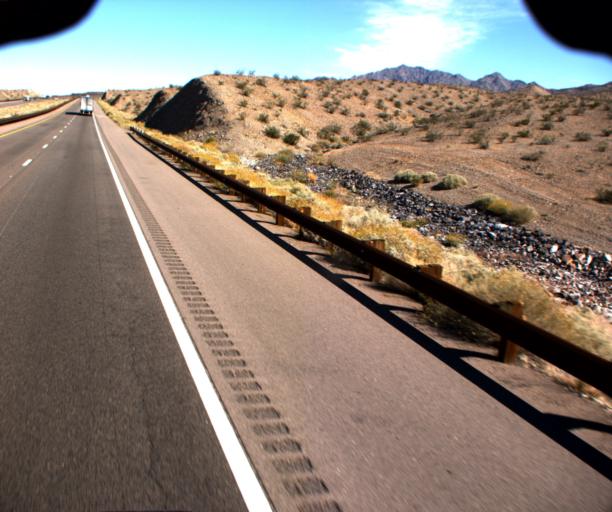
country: US
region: Nevada
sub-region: Clark County
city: Boulder City
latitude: 35.9204
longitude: -114.6311
